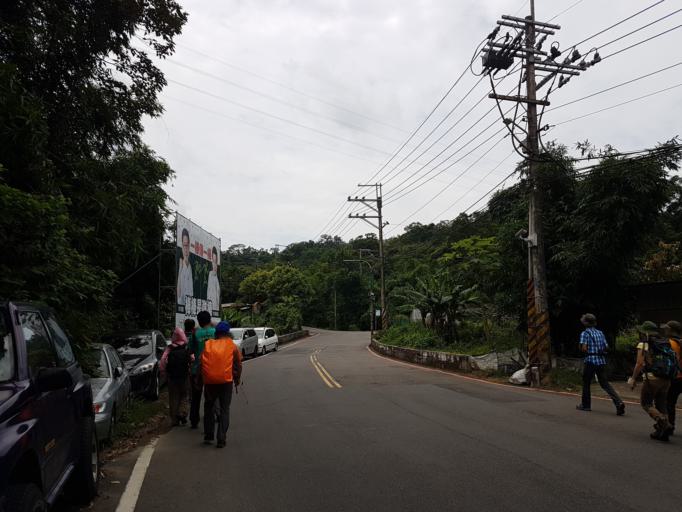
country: TW
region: Taiwan
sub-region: Keelung
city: Keelung
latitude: 25.0610
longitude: 121.6597
